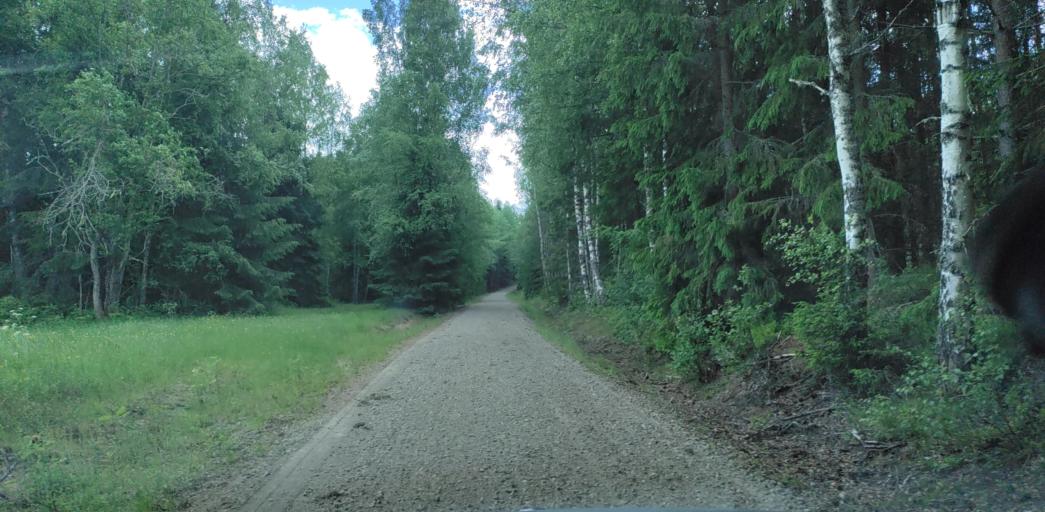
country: SE
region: Vaermland
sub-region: Munkfors Kommun
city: Munkfors
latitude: 59.9682
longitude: 13.4214
